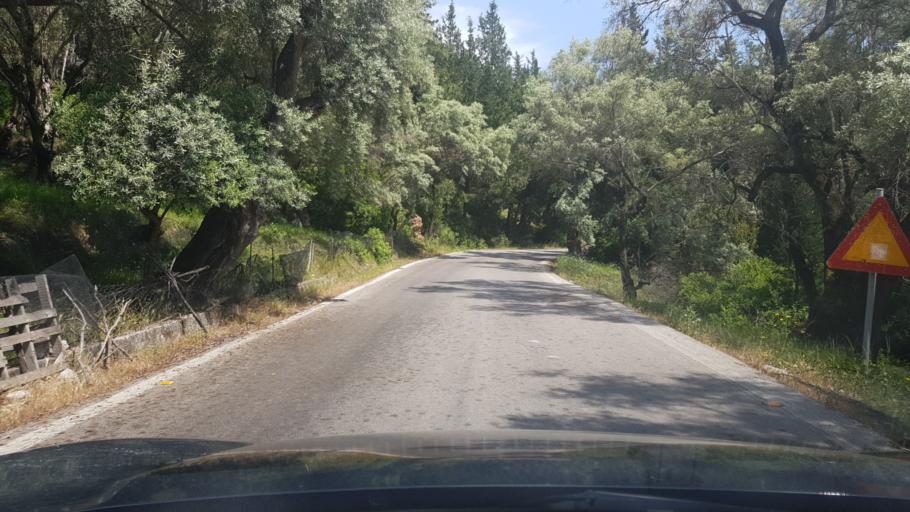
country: GR
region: Ionian Islands
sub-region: Lefkada
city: Nidri
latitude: 38.6535
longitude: 20.7040
